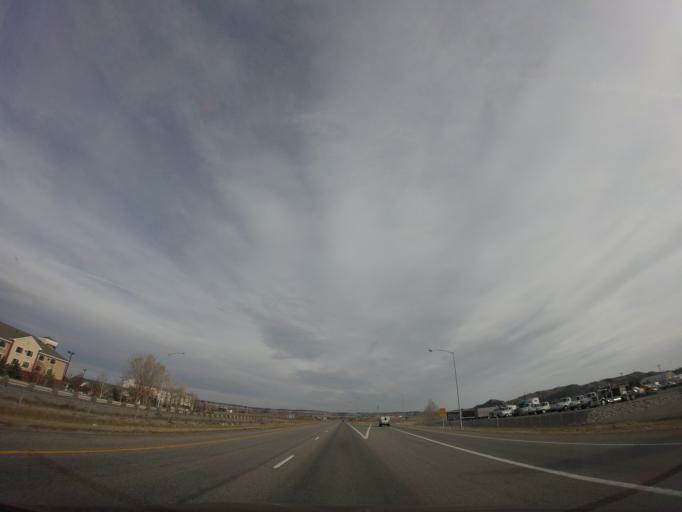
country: US
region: Montana
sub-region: Yellowstone County
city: Billings
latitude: 45.7521
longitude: -108.5408
